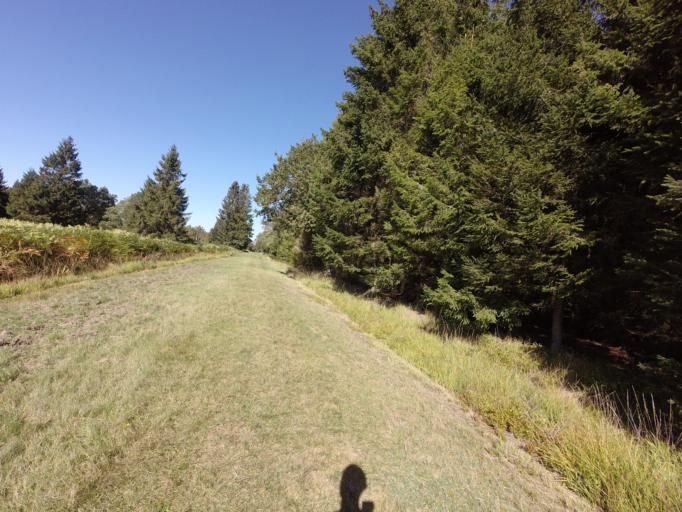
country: DE
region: North Rhine-Westphalia
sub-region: Regierungsbezirk Koln
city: Roetgen
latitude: 50.5968
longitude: 6.1756
